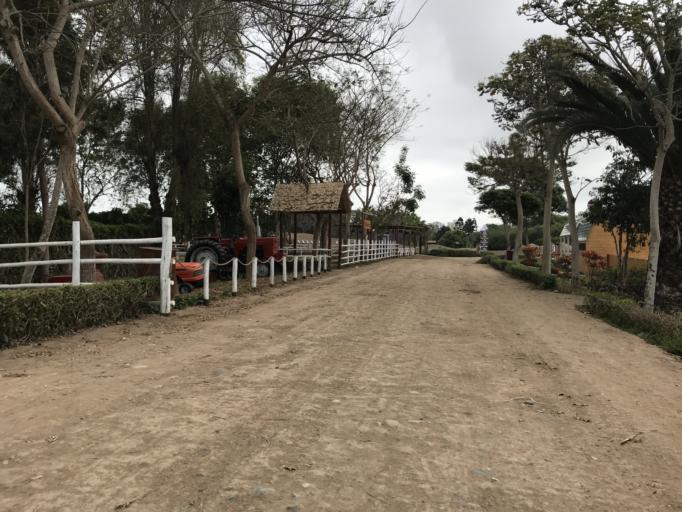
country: PE
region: Callao
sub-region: Callao
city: Callao
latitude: -12.0665
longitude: -77.0859
